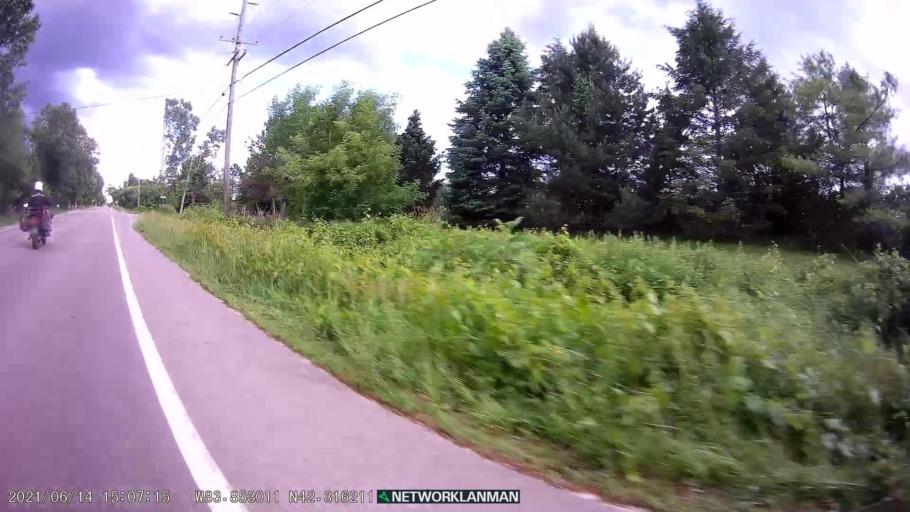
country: US
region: Michigan
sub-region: Washtenaw County
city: Dexter
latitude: 42.3161
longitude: -83.8528
